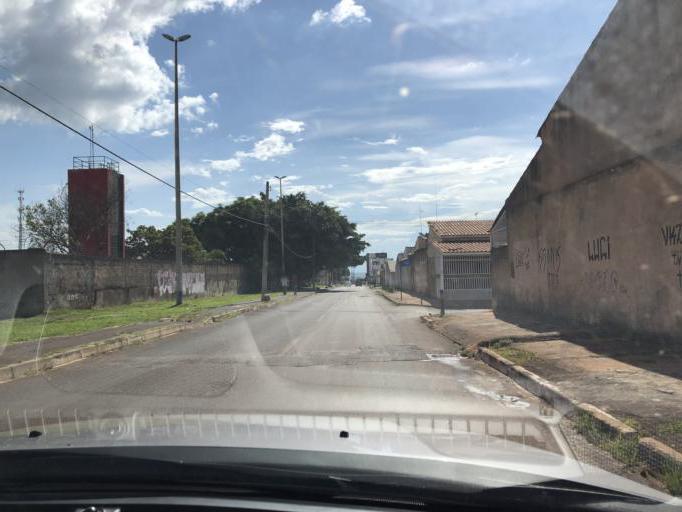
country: BR
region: Federal District
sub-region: Brasilia
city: Brasilia
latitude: -15.7980
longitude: -48.1265
